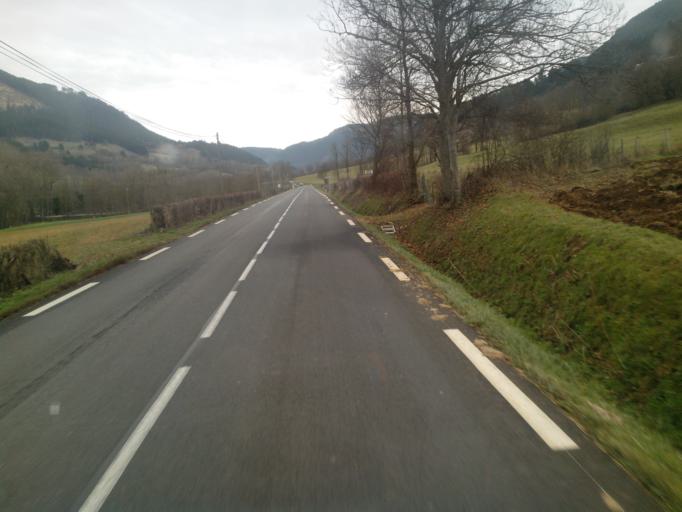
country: FR
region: Languedoc-Roussillon
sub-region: Departement de la Lozere
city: Mende
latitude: 44.4735
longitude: 3.5029
